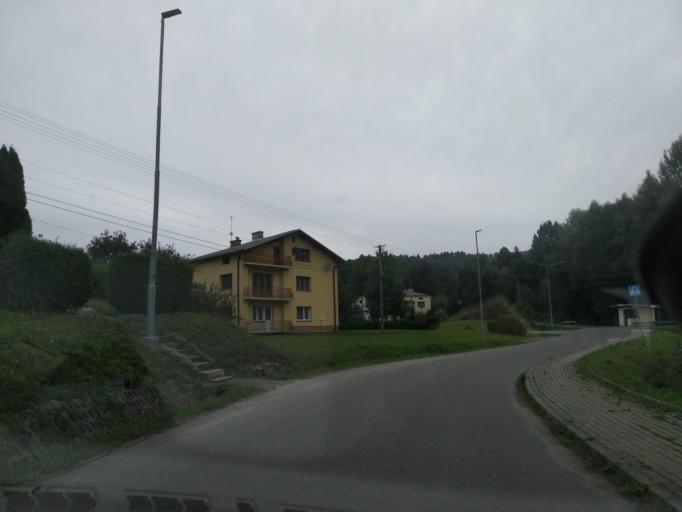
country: PL
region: Subcarpathian Voivodeship
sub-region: Powiat krosnienski
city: Korczyna
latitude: 49.7268
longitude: 21.8292
